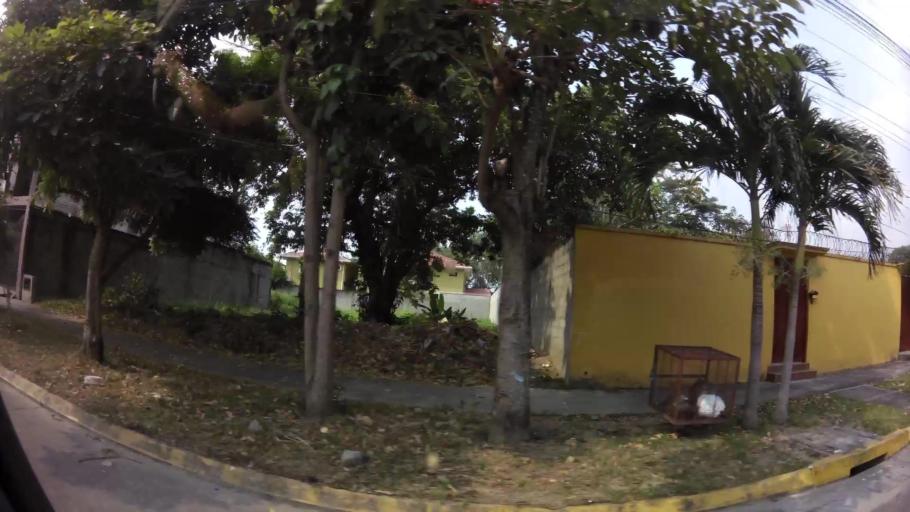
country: HN
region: Cortes
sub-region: San Pedro Sula
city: Pena Blanca
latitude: 15.5362
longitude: -88.0223
